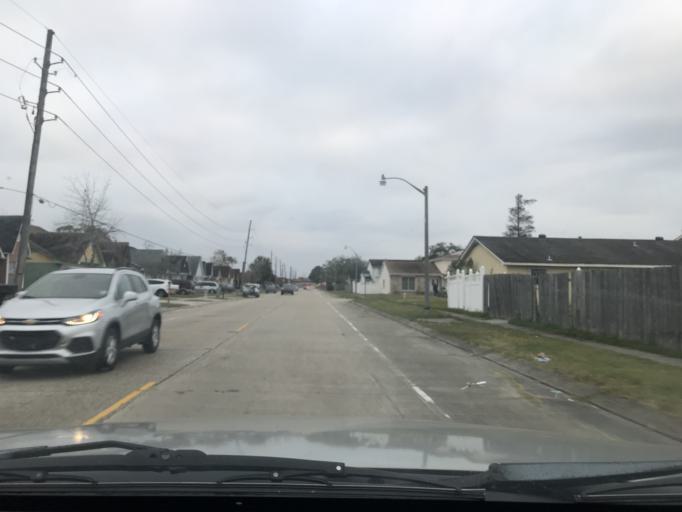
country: US
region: Louisiana
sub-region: Jefferson Parish
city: Woodmere
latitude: 29.8596
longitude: -90.0742
